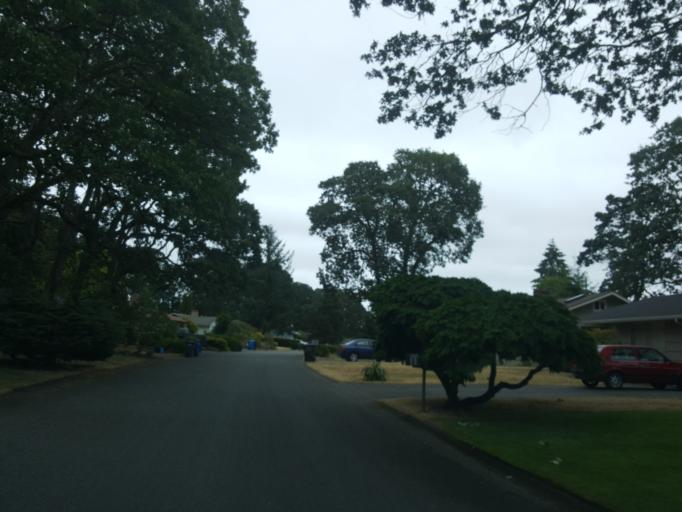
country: US
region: Washington
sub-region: Pierce County
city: Lakewood
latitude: 47.1643
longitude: -122.4895
